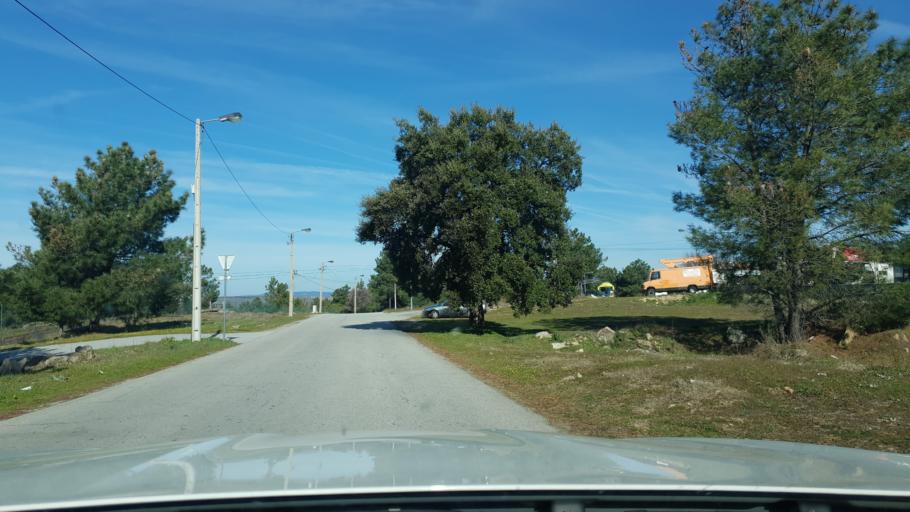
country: PT
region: Braganca
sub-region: Torre de Moncorvo
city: Torre de Moncorvo
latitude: 41.1907
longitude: -7.0191
